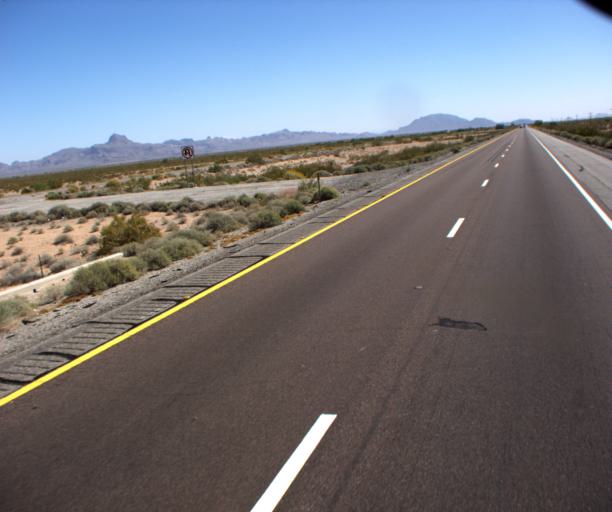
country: US
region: Arizona
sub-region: La Paz County
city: Salome
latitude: 33.5570
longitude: -113.2761
